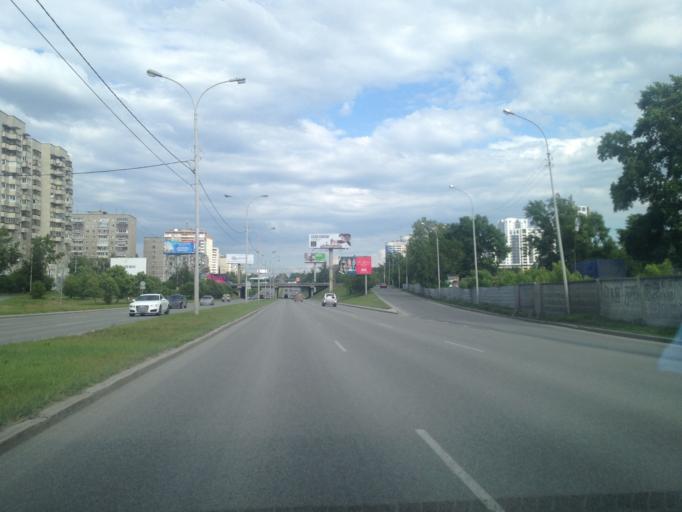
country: RU
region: Sverdlovsk
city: Shirokaya Rechka
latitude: 56.8266
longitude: 60.5389
